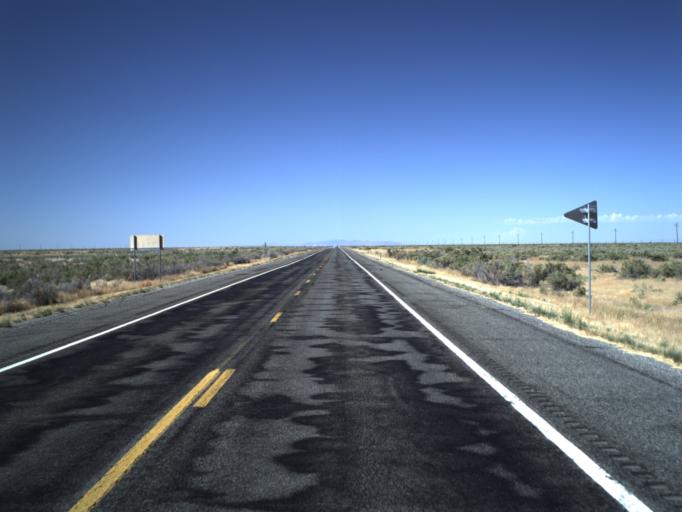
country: US
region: Utah
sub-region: Millard County
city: Delta
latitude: 39.4586
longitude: -112.4367
